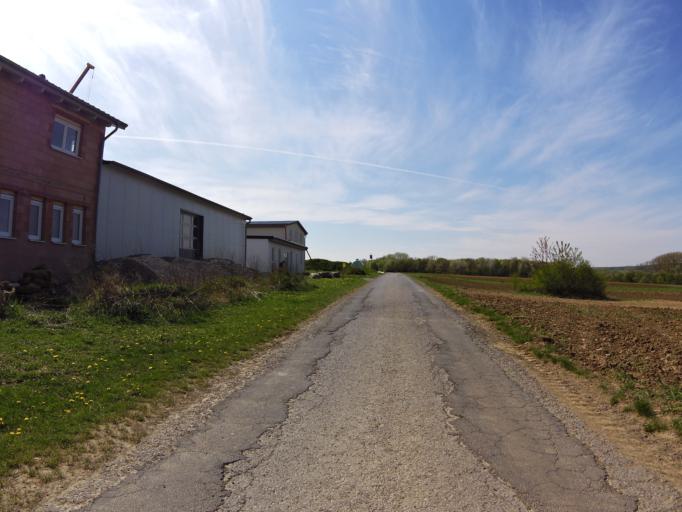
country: DE
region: Bavaria
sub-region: Regierungsbezirk Unterfranken
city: Unterpleichfeld
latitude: 49.8656
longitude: 10.0390
